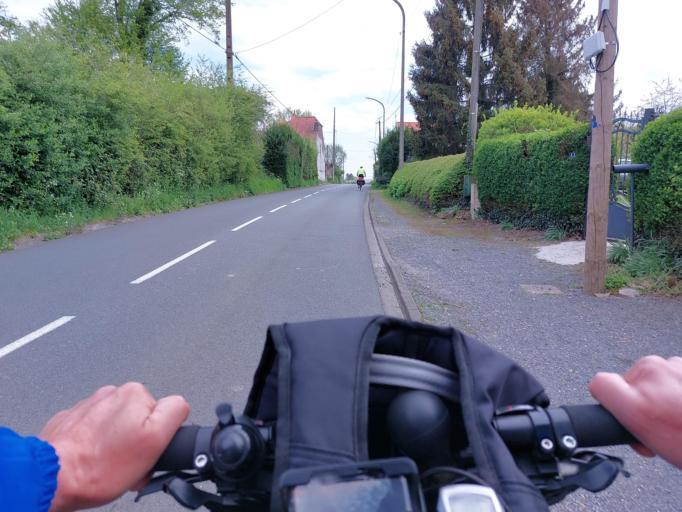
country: FR
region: Nord-Pas-de-Calais
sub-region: Departement du Nord
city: Hautmont
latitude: 50.2682
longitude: 3.8948
